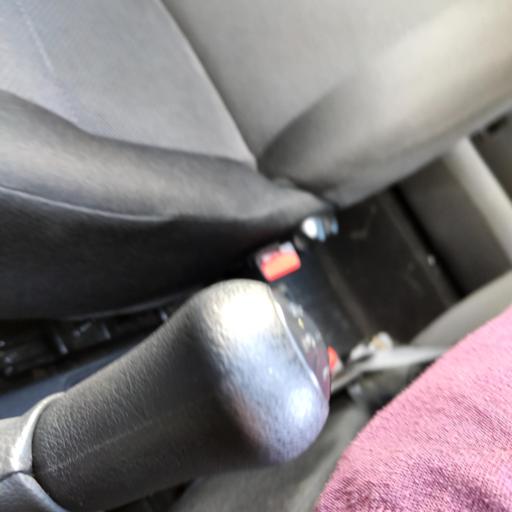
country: RU
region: Voronezj
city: Pridonskoy
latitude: 51.6209
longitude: 39.0605
